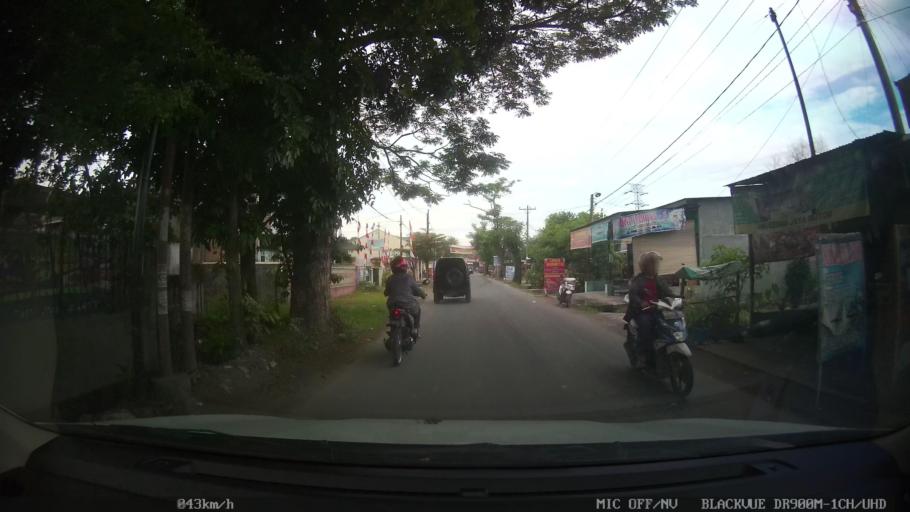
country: ID
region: North Sumatra
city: Sunggal
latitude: 3.6189
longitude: 98.6033
